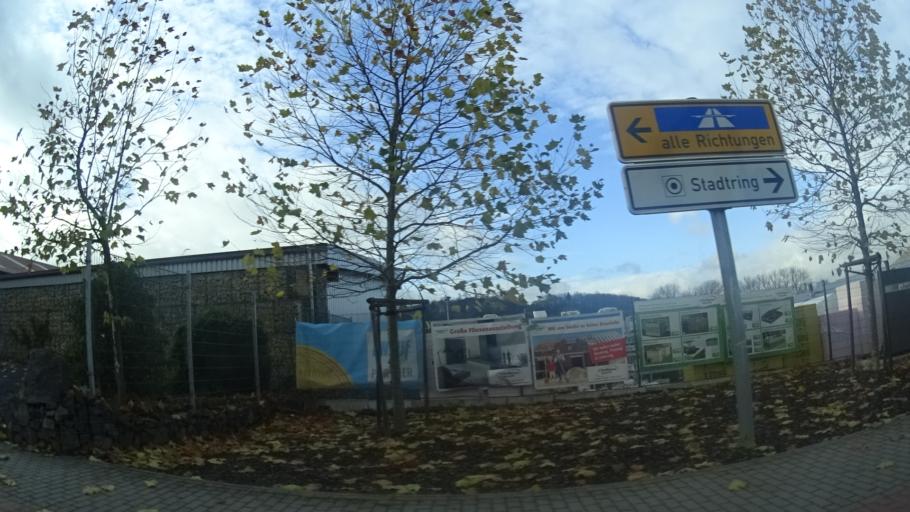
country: DE
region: Hesse
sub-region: Regierungsbezirk Kassel
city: Hunfeld
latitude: 50.6661
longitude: 9.7609
